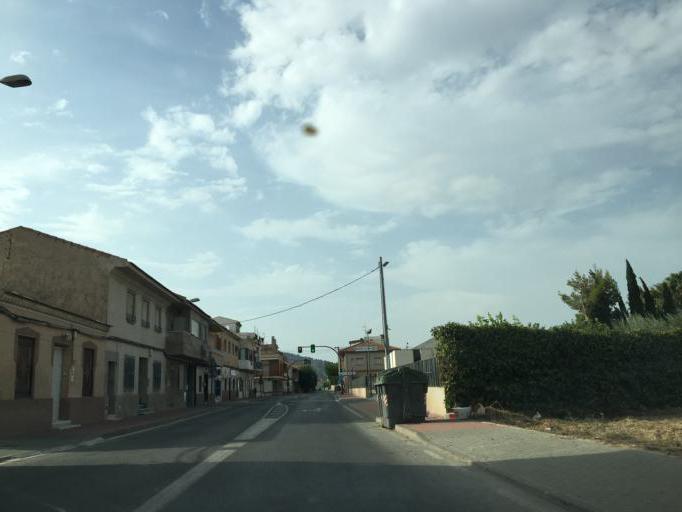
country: ES
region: Murcia
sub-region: Murcia
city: Murcia
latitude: 38.0126
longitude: -1.0818
